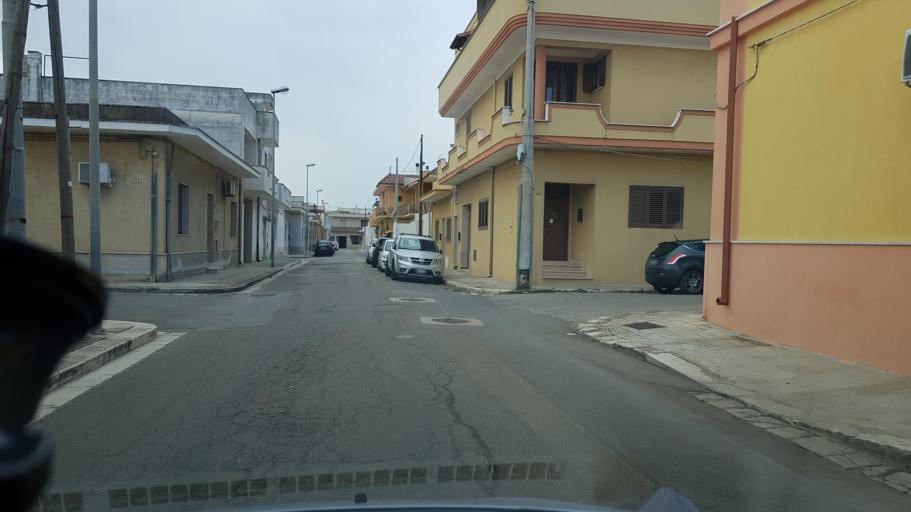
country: IT
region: Apulia
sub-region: Provincia di Brindisi
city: Mesagne
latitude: 40.5493
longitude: 17.8093
